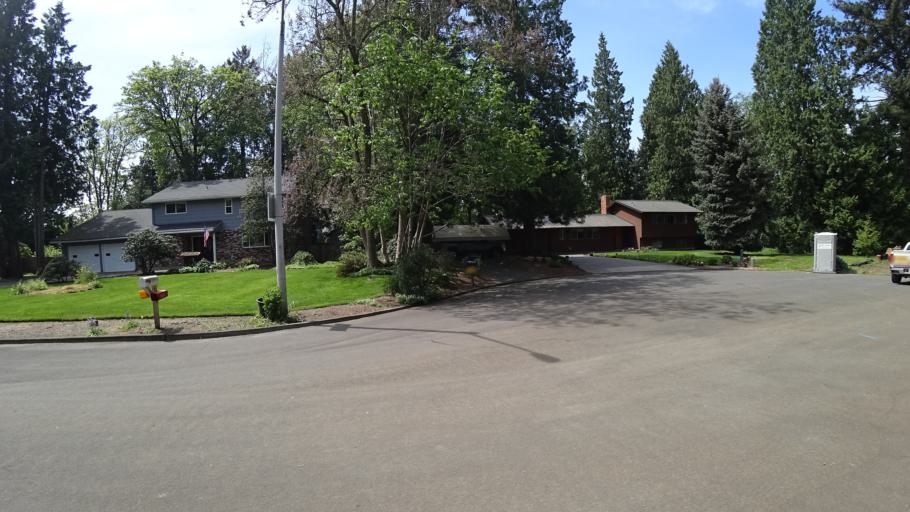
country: US
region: Oregon
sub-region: Washington County
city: Rockcreek
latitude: 45.5161
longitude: -122.9217
